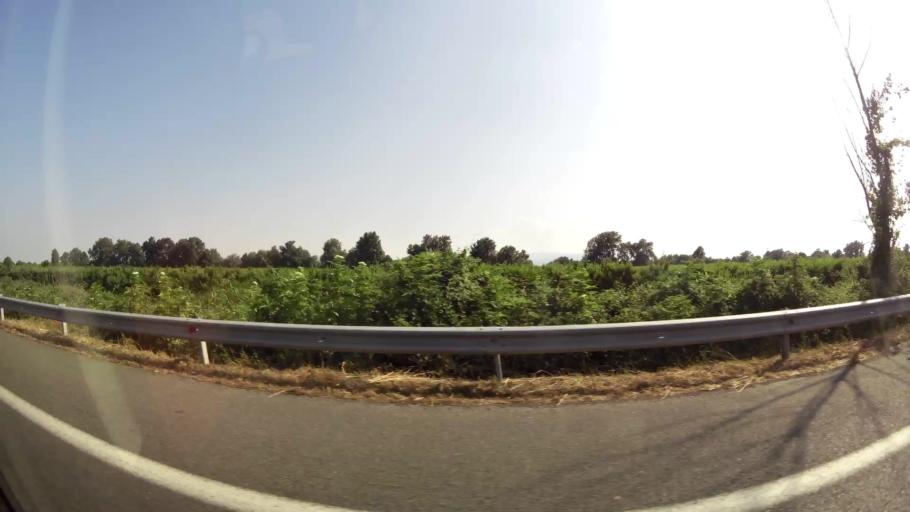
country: GR
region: Central Macedonia
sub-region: Nomos Imathias
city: Koryfi
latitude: 40.5836
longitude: 22.4832
